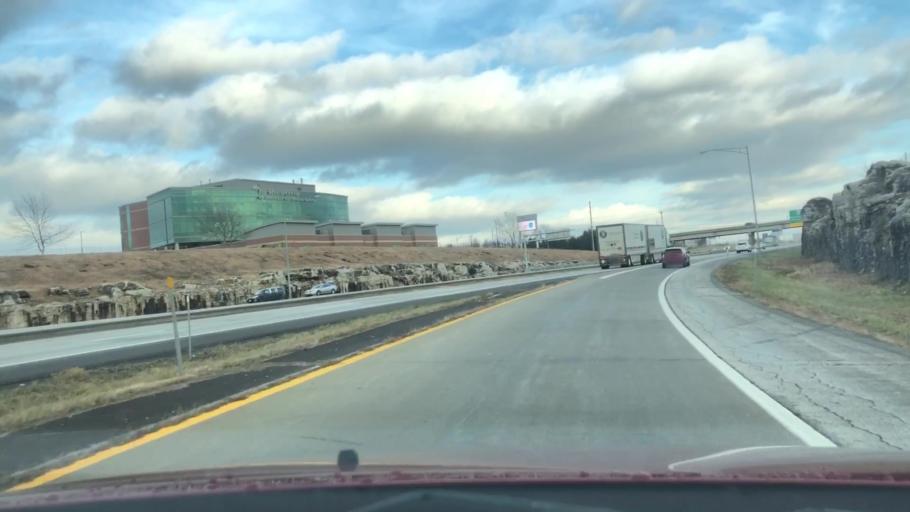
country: US
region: Missouri
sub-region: Greene County
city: Springfield
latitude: 37.1419
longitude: -93.2754
